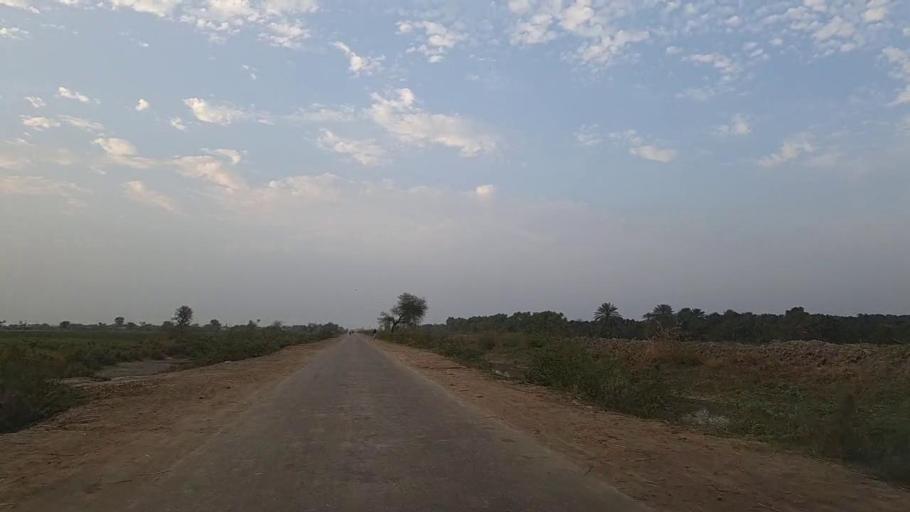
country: PK
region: Sindh
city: Mirwah Gorchani
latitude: 25.3208
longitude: 69.2196
